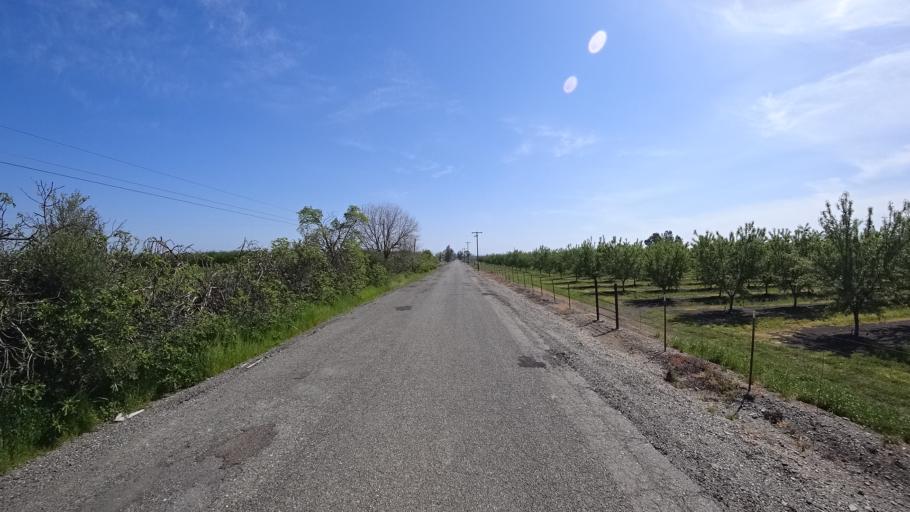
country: US
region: California
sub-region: Glenn County
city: Hamilton City
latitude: 39.8042
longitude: -122.0888
